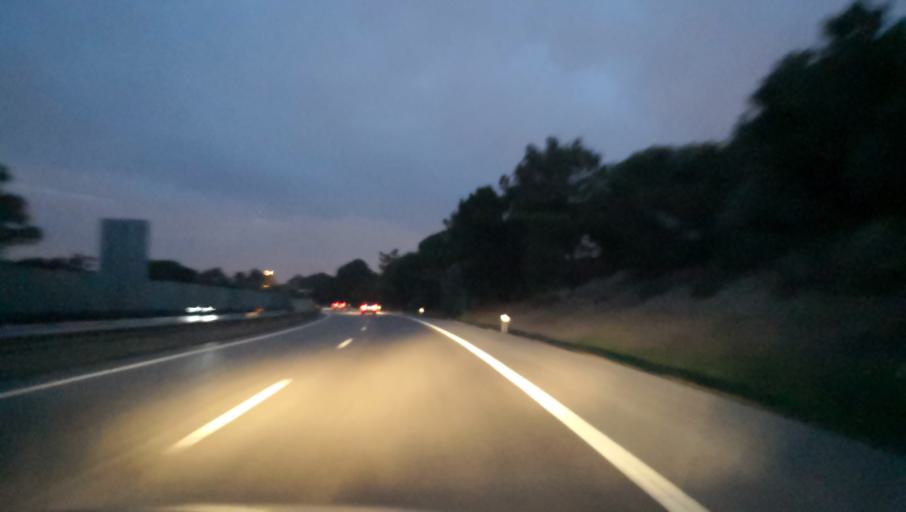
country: PT
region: Setubal
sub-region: Barreiro
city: Santo Antonio da Charneca
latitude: 38.6288
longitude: -9.0385
